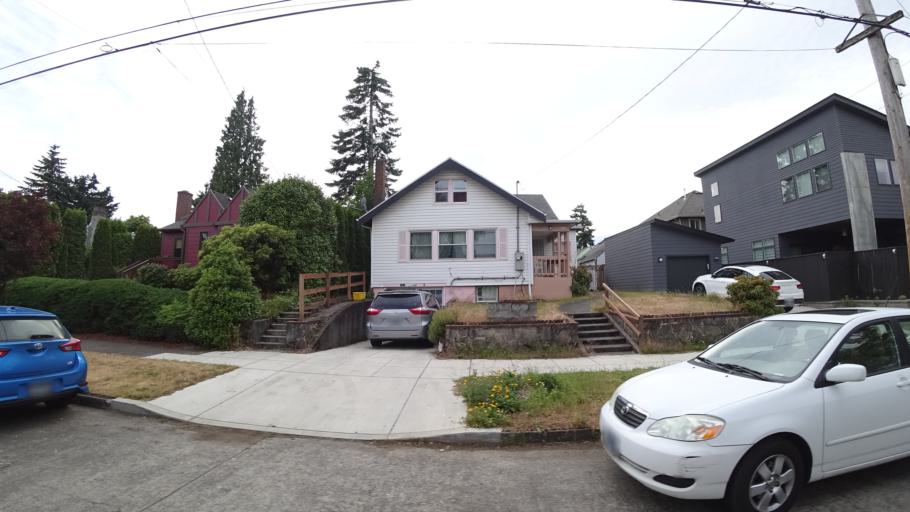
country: US
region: Oregon
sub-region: Multnomah County
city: Portland
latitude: 45.5713
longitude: -122.6833
